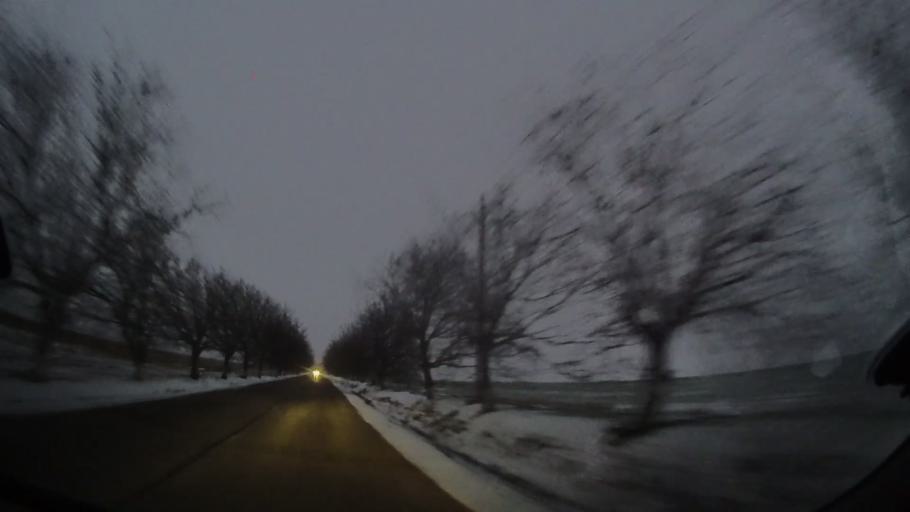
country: RO
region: Vaslui
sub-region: Comuna Dimitrie Cantemir
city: Dimitrie Cantemir
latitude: 46.5120
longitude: 28.0343
